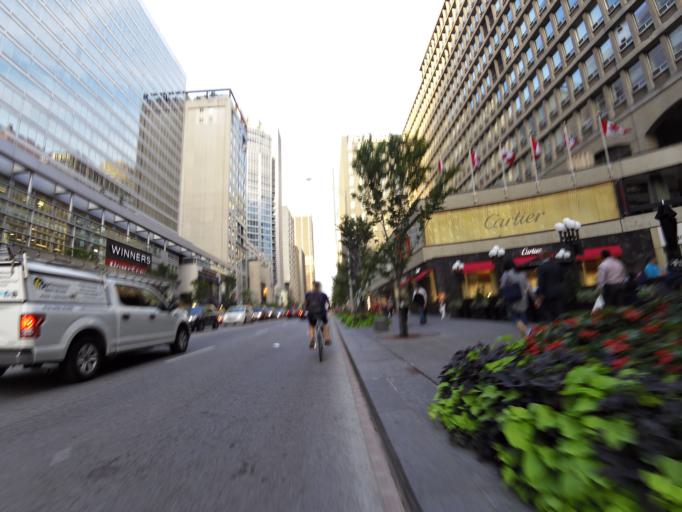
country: CA
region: Ontario
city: Toronto
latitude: 43.6691
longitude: -79.3926
